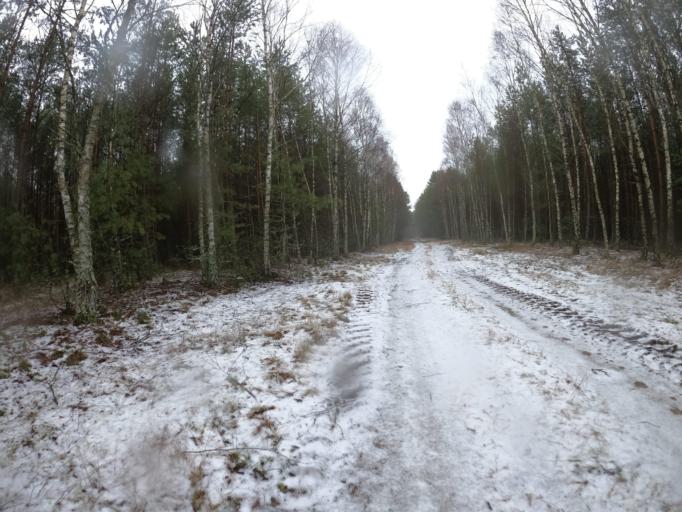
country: PL
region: Lubusz
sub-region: Powiat slubicki
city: Cybinka
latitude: 52.2029
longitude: 14.9274
